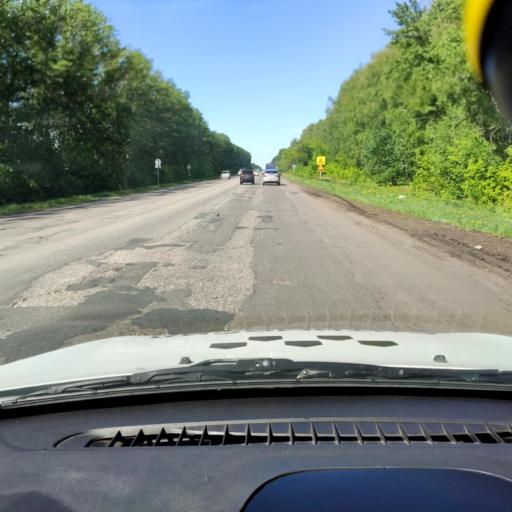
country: RU
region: Samara
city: Tol'yatti
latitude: 53.6224
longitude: 49.4151
